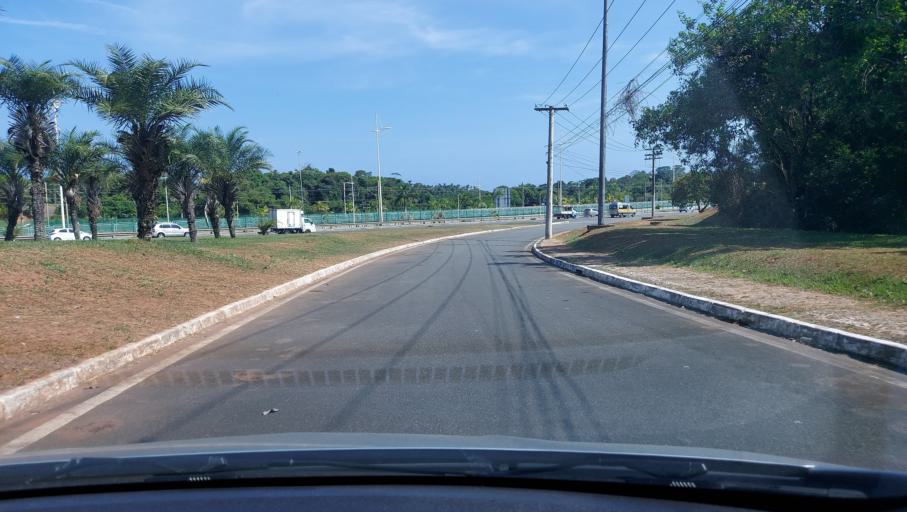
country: BR
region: Bahia
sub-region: Salvador
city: Salvador
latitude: -12.9499
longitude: -38.4260
